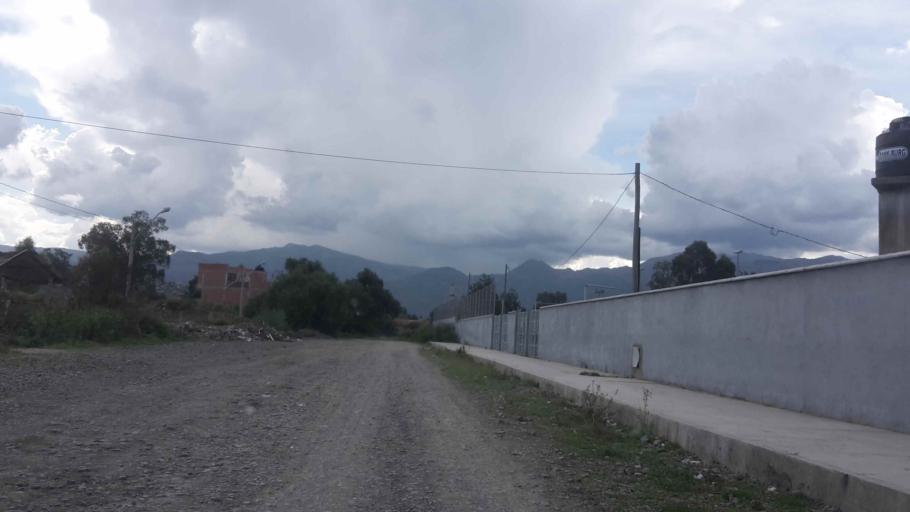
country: BO
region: Cochabamba
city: Sipe Sipe
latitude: -17.4087
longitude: -66.2895
